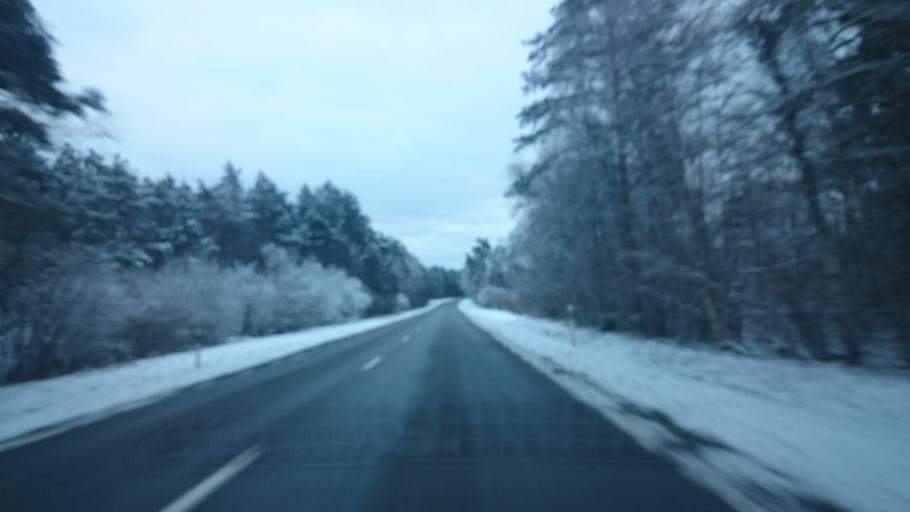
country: EE
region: Saare
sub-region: Kuressaare linn
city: Kuressaare
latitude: 58.3970
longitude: 22.6446
